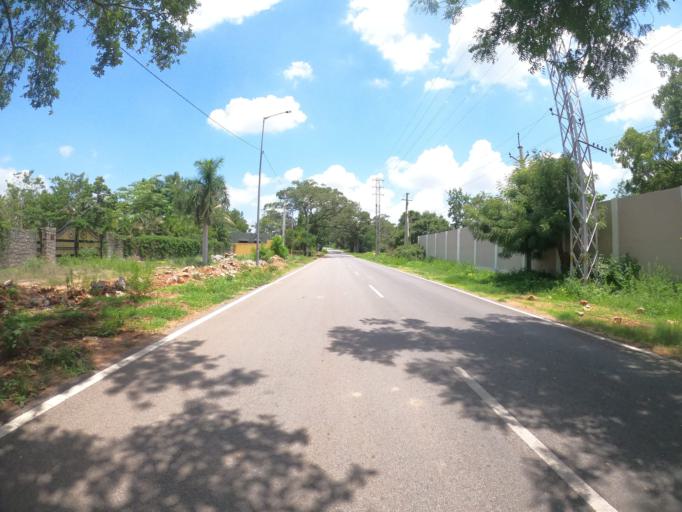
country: IN
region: Telangana
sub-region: Rangareddi
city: Sriramnagar
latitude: 17.3643
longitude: 78.3239
